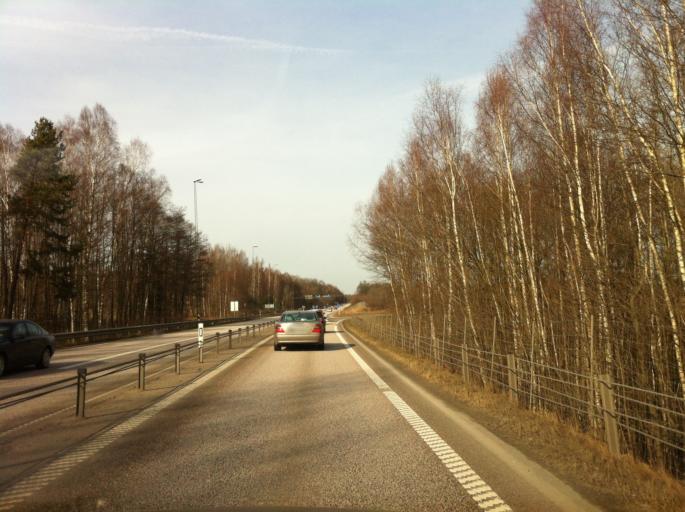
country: SE
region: Vaestra Goetaland
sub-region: Skovde Kommun
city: Stopen
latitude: 58.4492
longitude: 13.8503
